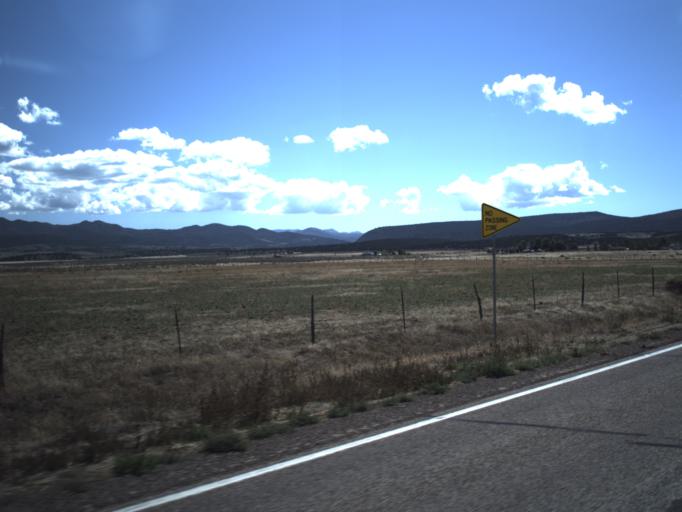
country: US
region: Utah
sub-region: Washington County
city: Enterprise
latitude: 37.6074
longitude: -113.6612
